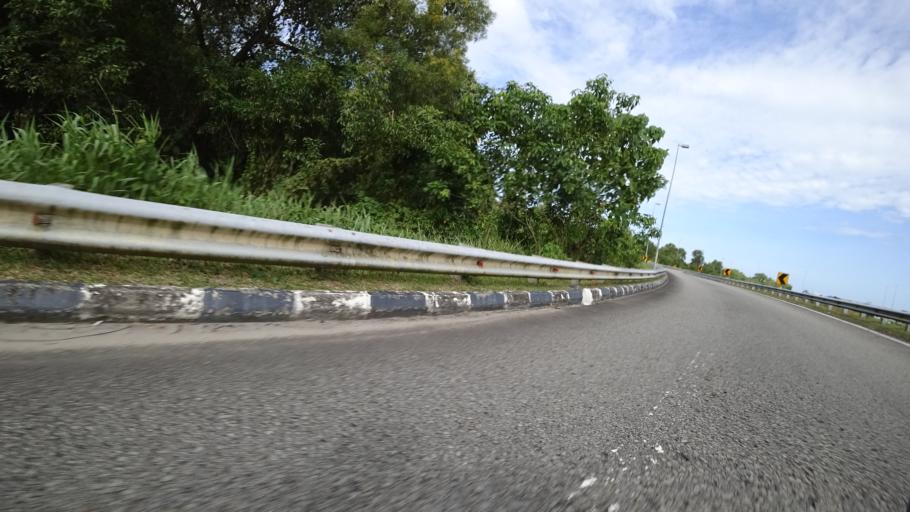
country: BN
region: Brunei and Muara
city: Bandar Seri Begawan
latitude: 4.9224
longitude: 114.9110
